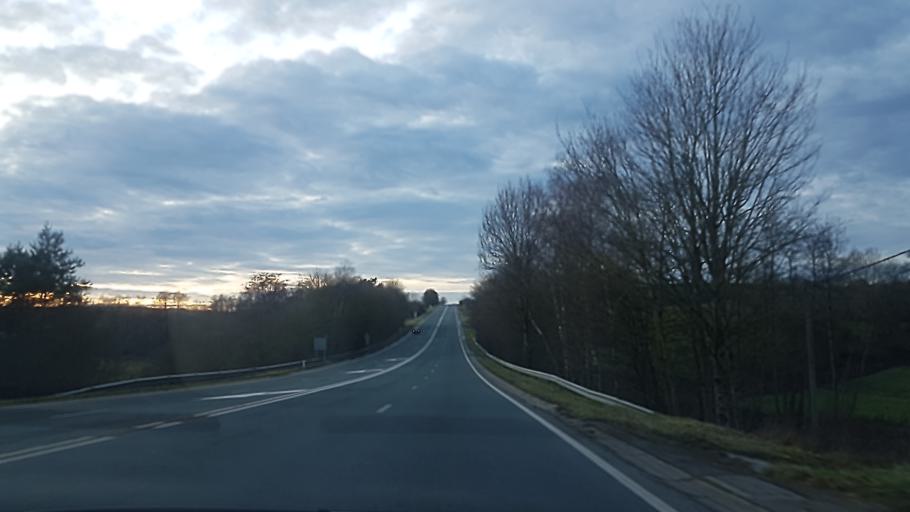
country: BE
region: Wallonia
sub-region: Province de Namur
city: Couvin
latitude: 50.0482
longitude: 4.4483
